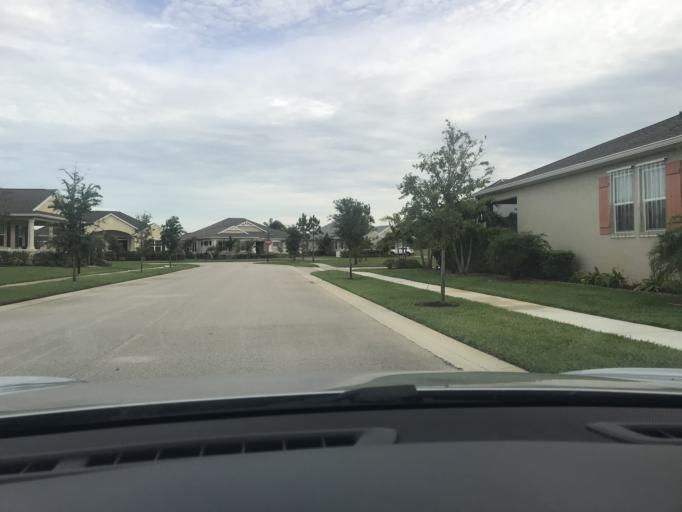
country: US
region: Florida
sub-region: Indian River County
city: West Vero Corridor
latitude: 27.6276
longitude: -80.4739
